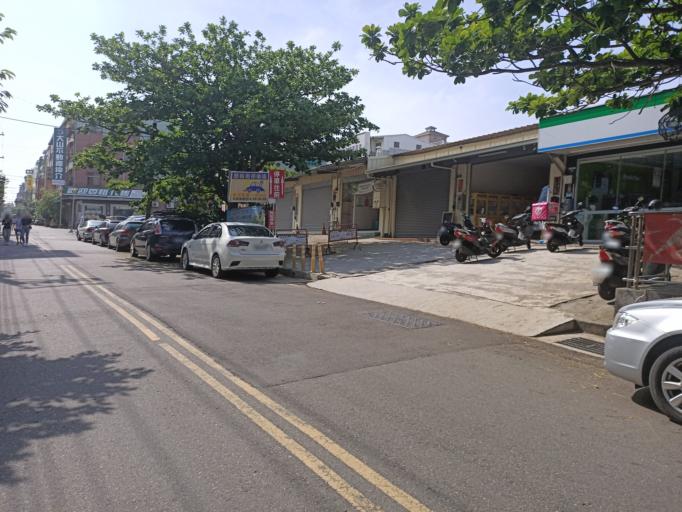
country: TW
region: Taiwan
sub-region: Taichung City
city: Taichung
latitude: 24.1881
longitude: 120.5925
